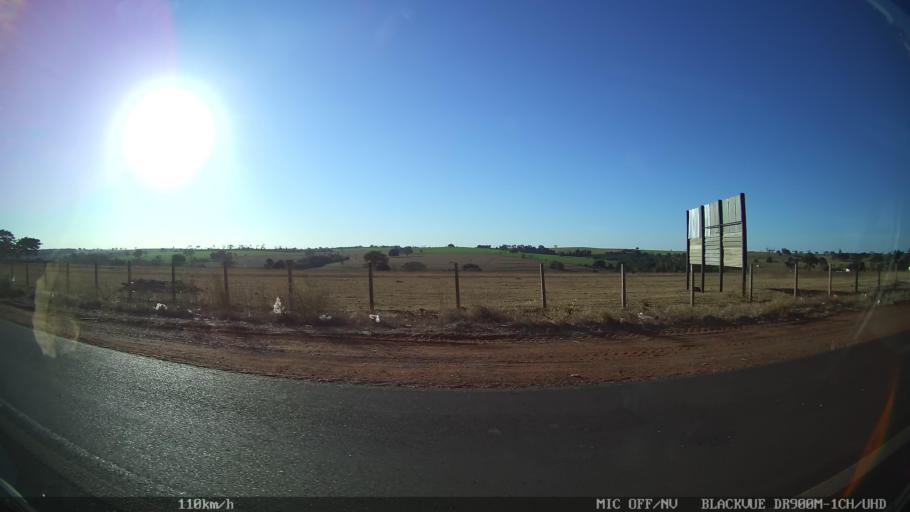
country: BR
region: Sao Paulo
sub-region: Guapiacu
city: Guapiacu
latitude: -20.7892
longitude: -49.2914
